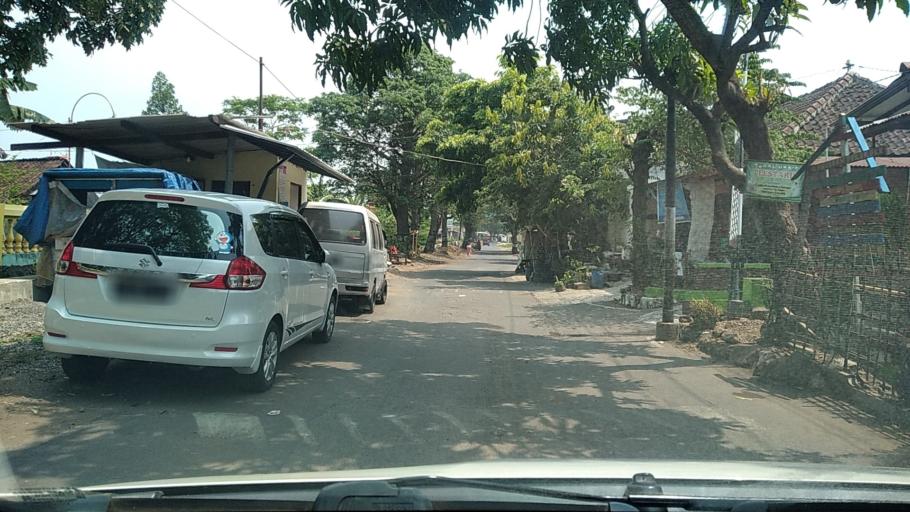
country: ID
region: Central Java
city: Semarang
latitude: -6.9837
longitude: 110.3635
